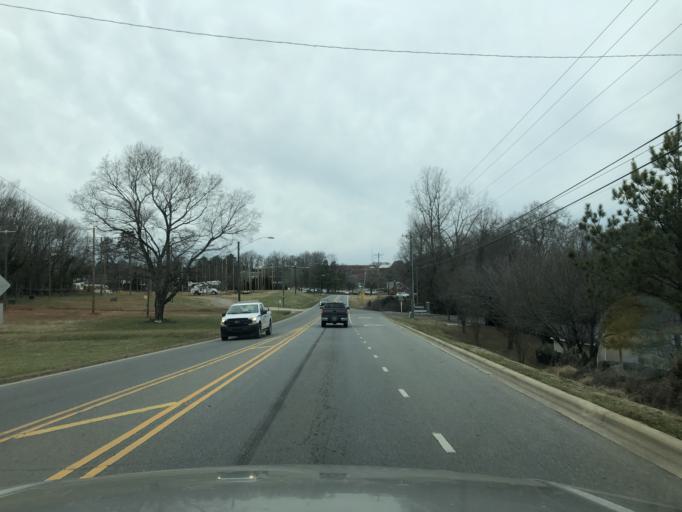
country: US
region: North Carolina
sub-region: Cleveland County
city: Shelby
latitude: 35.2759
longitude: -81.4855
